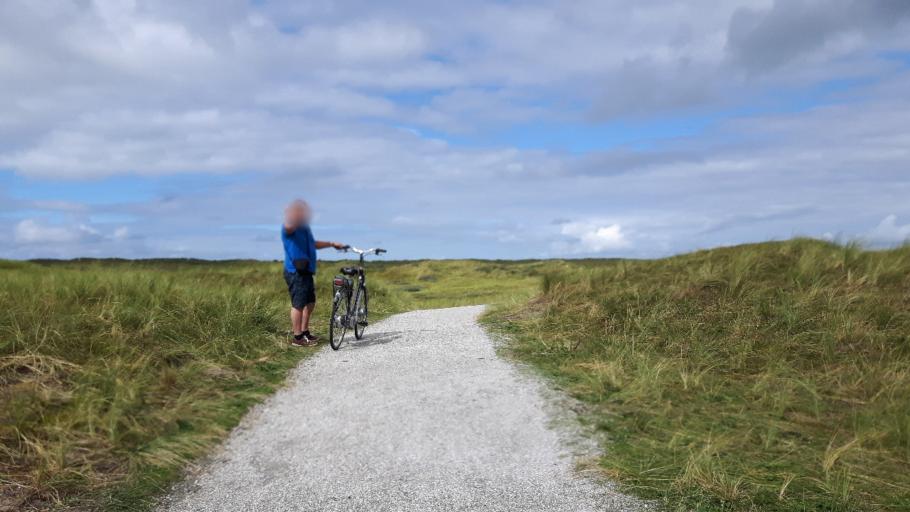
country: NL
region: Friesland
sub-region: Gemeente Ameland
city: Hollum
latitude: 53.4506
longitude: 5.6227
